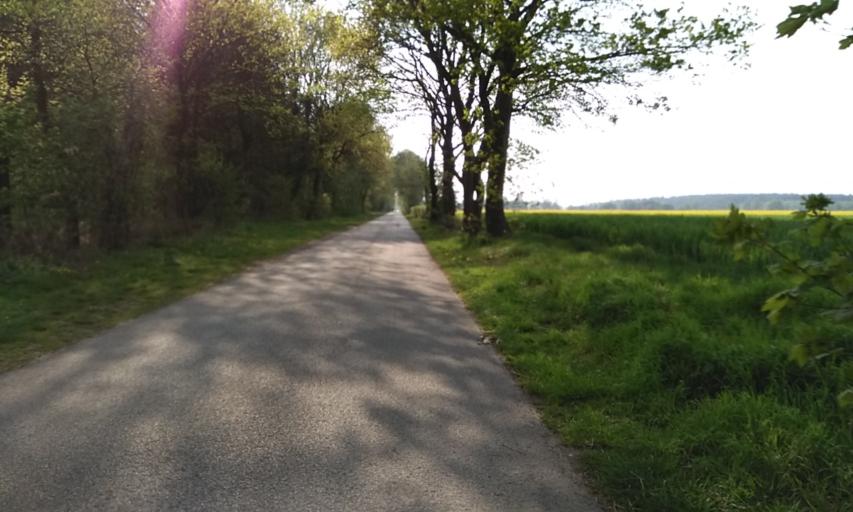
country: DE
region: Lower Saxony
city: Apensen
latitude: 53.4347
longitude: 9.6018
